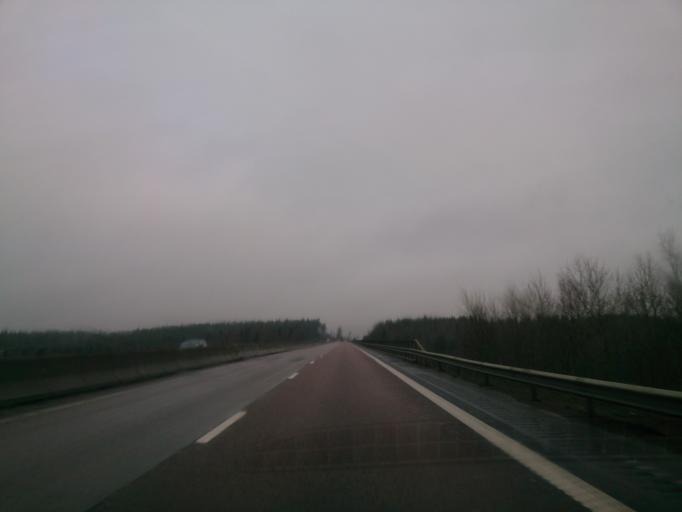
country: SE
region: OEstergoetland
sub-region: Norrkopings Kommun
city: Kimstad
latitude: 58.5087
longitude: 15.9915
